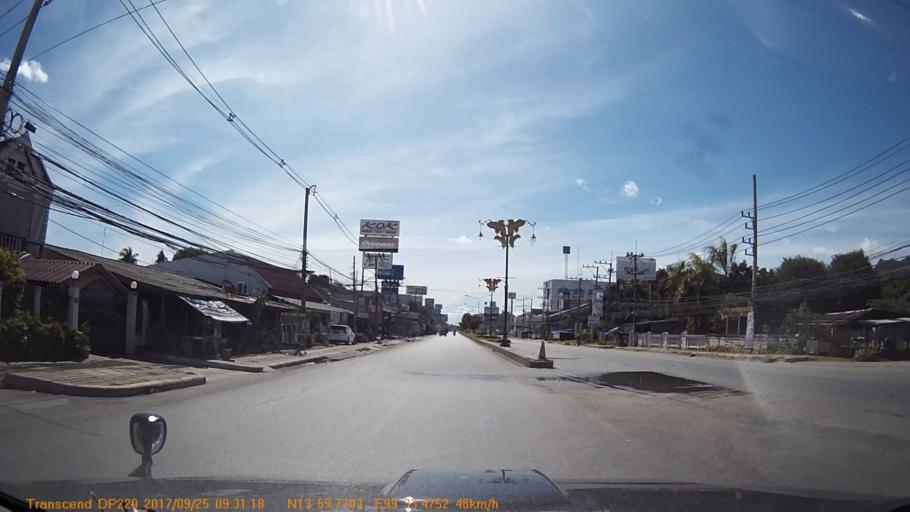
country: TH
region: Kanchanaburi
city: Kanchanaburi
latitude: 13.9961
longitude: 99.5580
